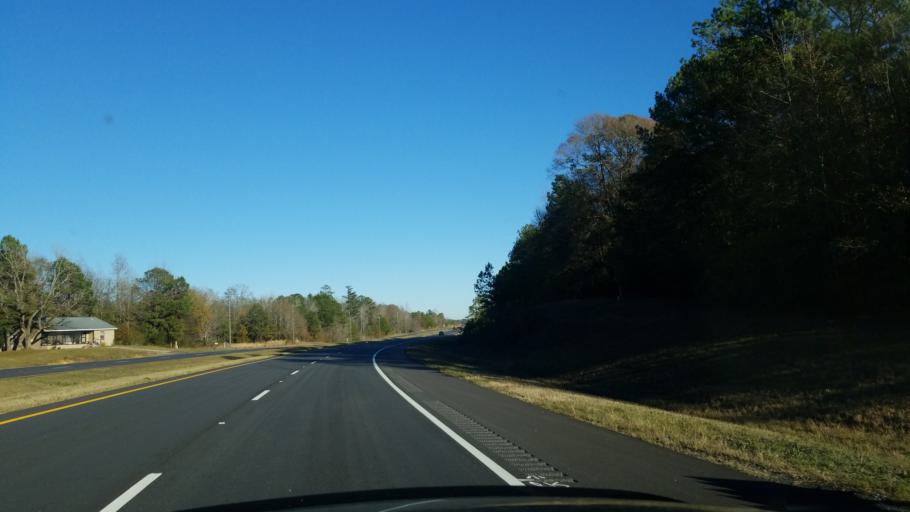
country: US
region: Georgia
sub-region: Talbot County
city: Talbotton
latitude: 32.5750
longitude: -84.5937
